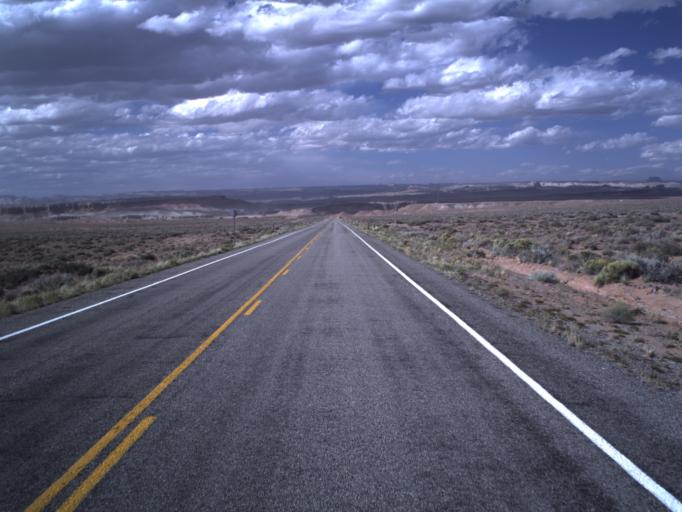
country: US
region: Utah
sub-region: Emery County
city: Ferron
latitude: 38.3415
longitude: -110.6911
